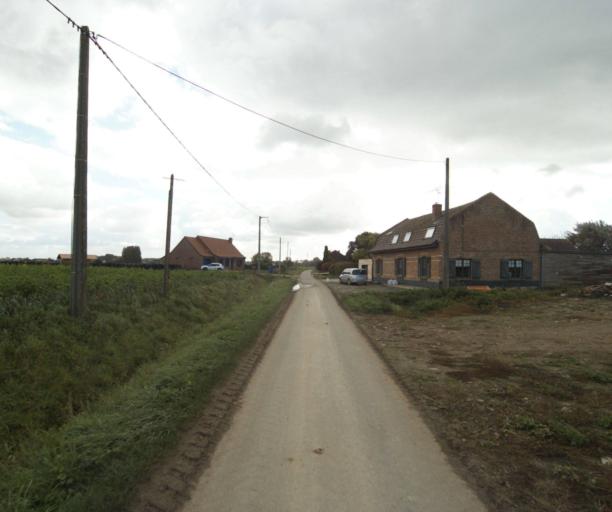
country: FR
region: Nord-Pas-de-Calais
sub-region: Departement du Nord
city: Perenchies
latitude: 50.6957
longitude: 2.9602
